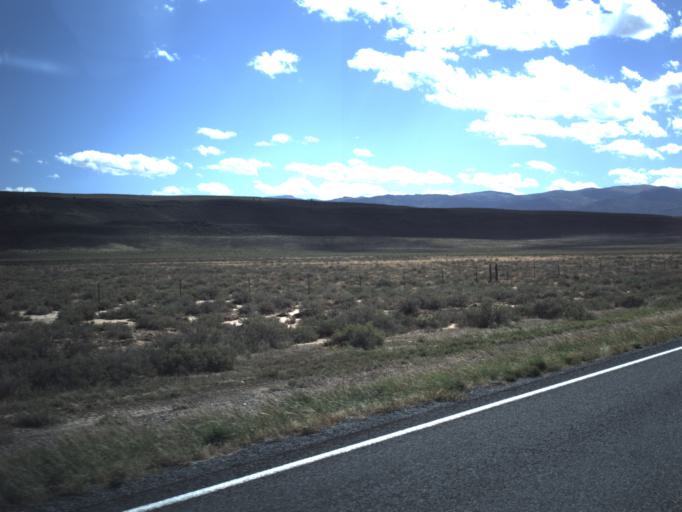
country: US
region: Utah
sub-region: Iron County
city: Enoch
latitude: 37.8721
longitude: -113.0316
